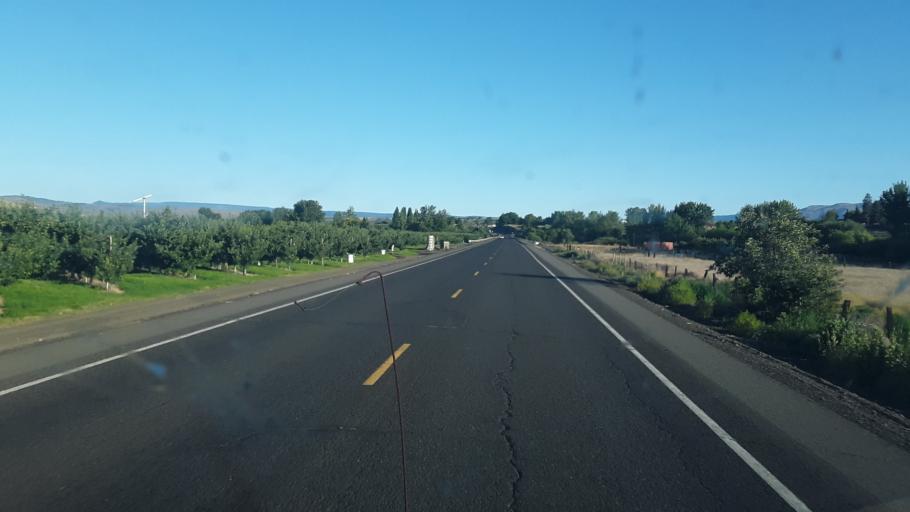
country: US
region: Washington
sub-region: Yakima County
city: Tieton
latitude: 46.6460
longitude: -120.6972
